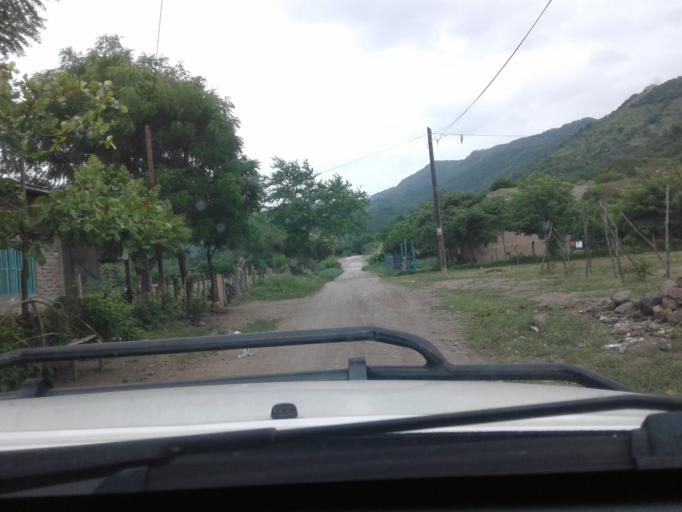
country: NI
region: Matagalpa
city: Ciudad Dario
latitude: 12.9023
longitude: -86.2038
